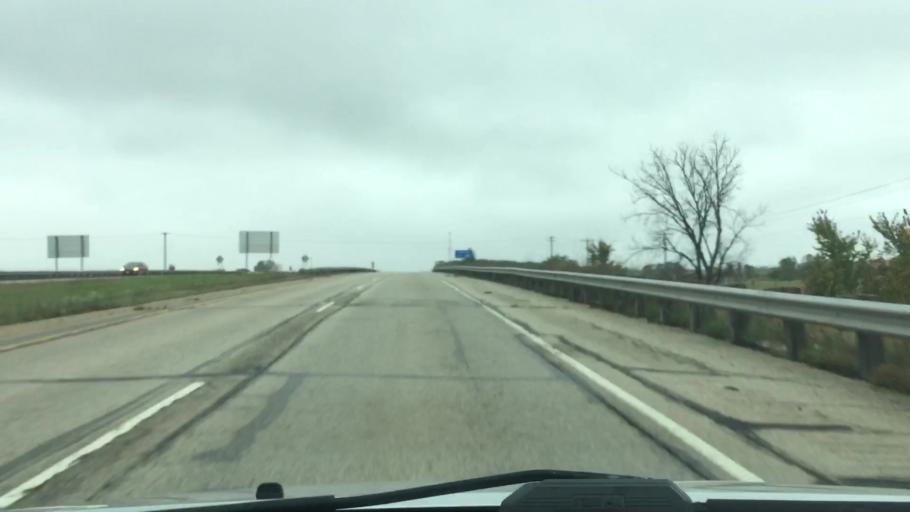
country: US
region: Wisconsin
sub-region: Walworth County
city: Elkhorn
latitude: 42.6846
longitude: -88.5292
